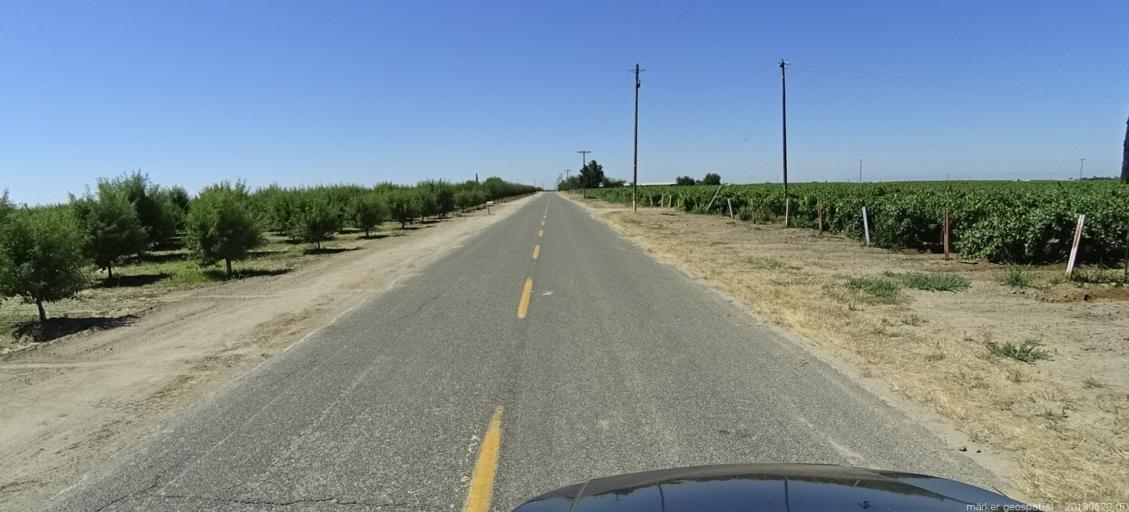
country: US
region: California
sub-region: Fresno County
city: Biola
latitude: 36.8485
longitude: -120.0192
